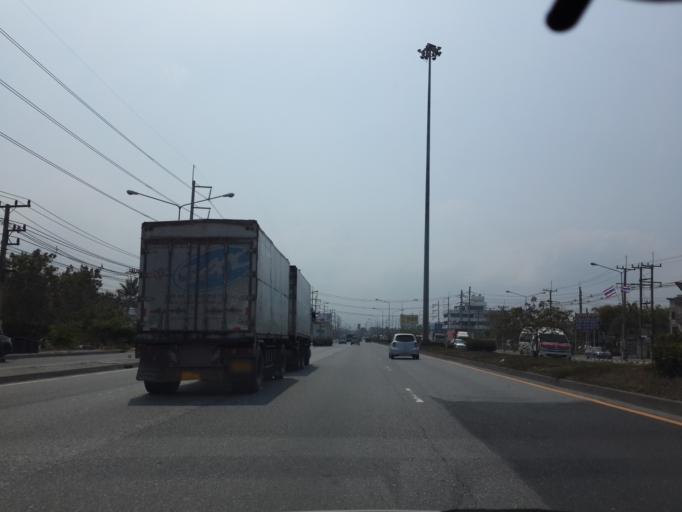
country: TH
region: Chon Buri
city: Chon Buri
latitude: 13.4119
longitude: 100.9998
